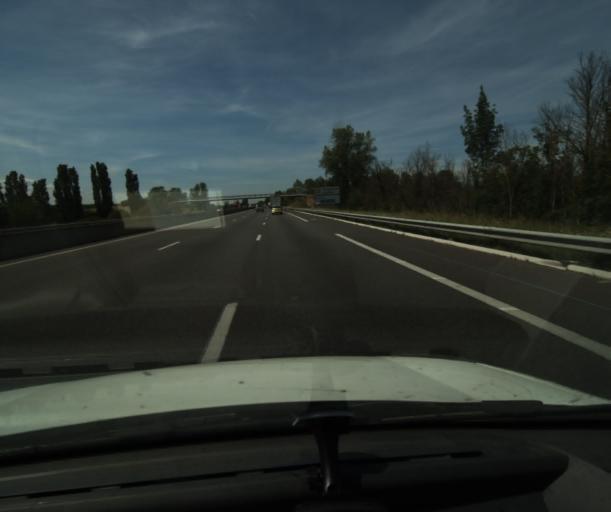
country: FR
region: Midi-Pyrenees
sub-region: Departement de la Haute-Garonne
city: Labege
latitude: 43.5296
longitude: 1.5154
